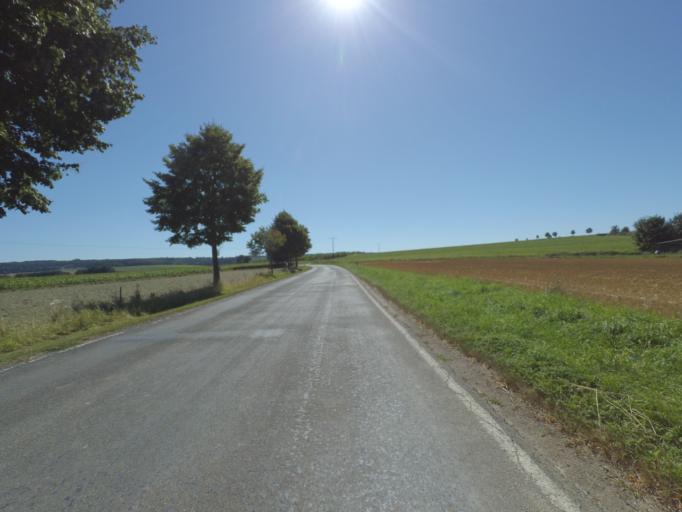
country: DE
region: Rheinland-Pfalz
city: Schmitt
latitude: 50.1644
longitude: 7.0175
